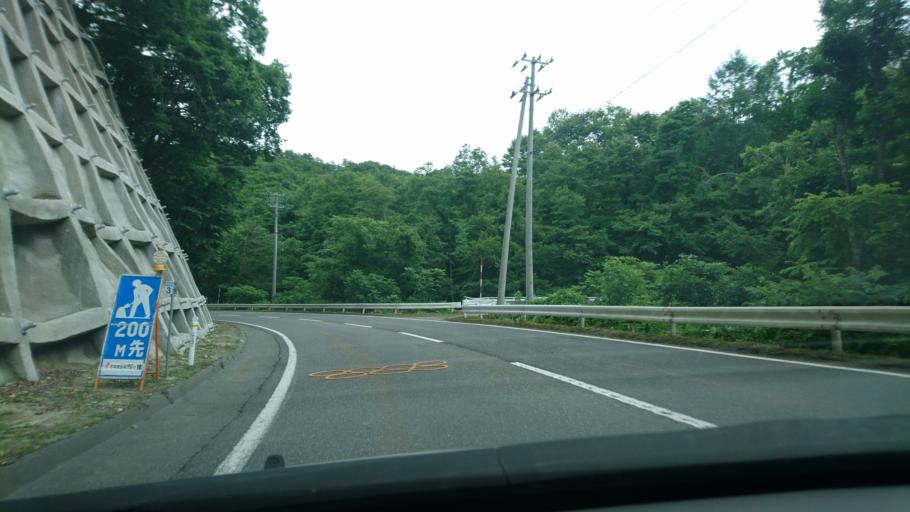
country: JP
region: Iwate
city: Miyako
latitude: 39.9672
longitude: 141.8586
